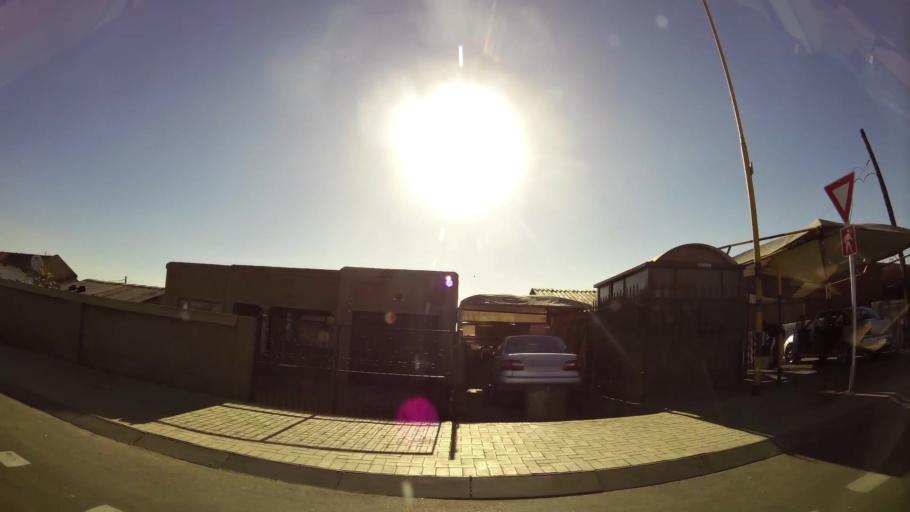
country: ZA
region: Gauteng
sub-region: Ekurhuleni Metropolitan Municipality
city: Tembisa
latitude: -26.0236
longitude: 28.2212
